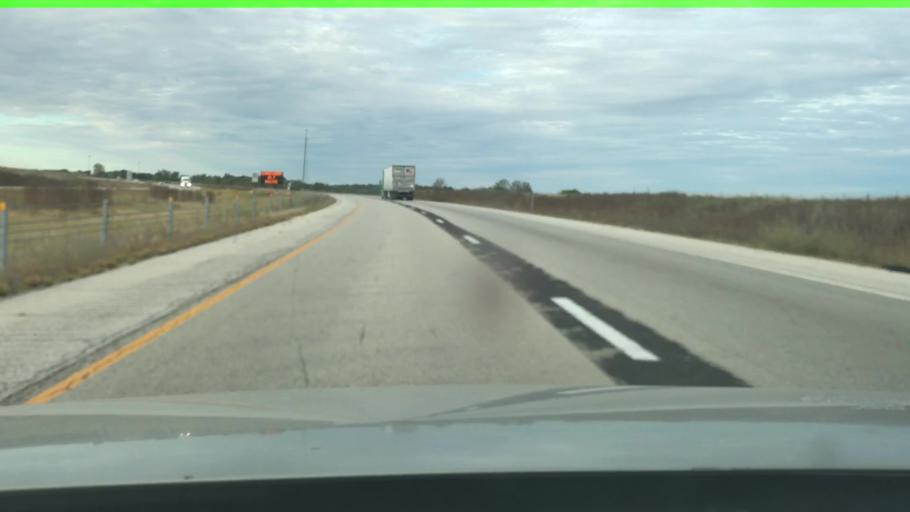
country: US
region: Illinois
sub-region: Livingston County
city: Odell
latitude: 41.0178
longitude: -88.5312
